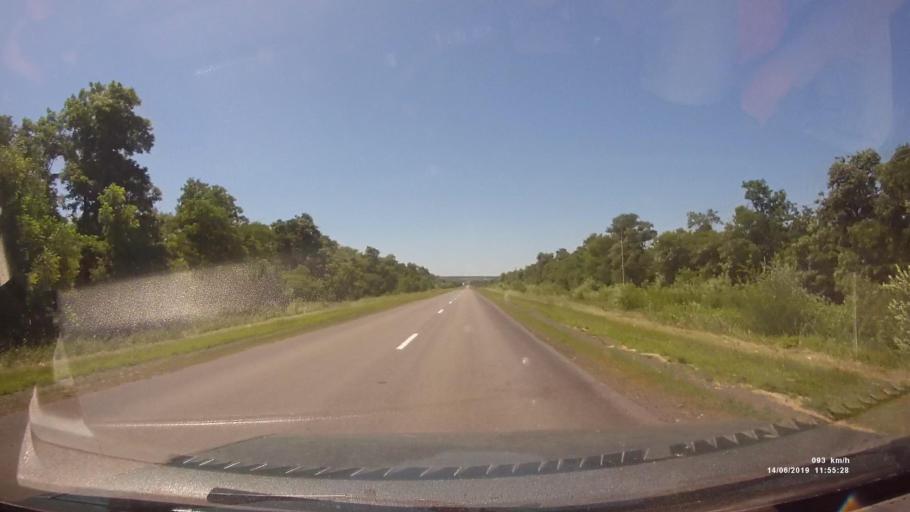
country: RU
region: Rostov
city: Kazanskaya
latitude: 49.8102
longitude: 41.1765
